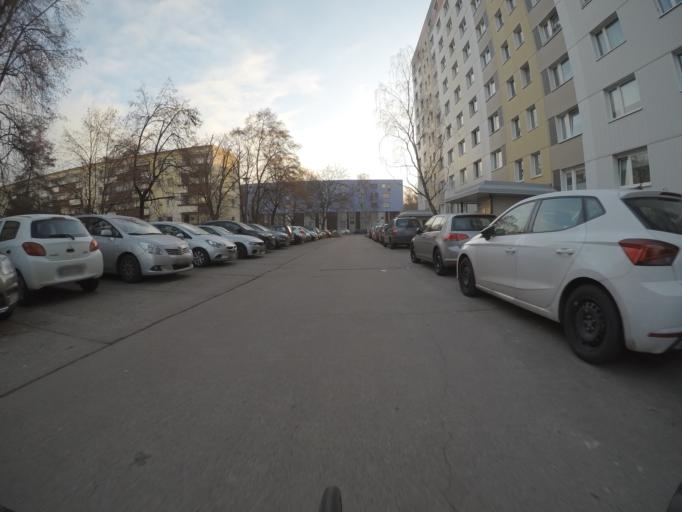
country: DE
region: Berlin
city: Friedrichsfelde
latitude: 52.4952
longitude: 13.5079
